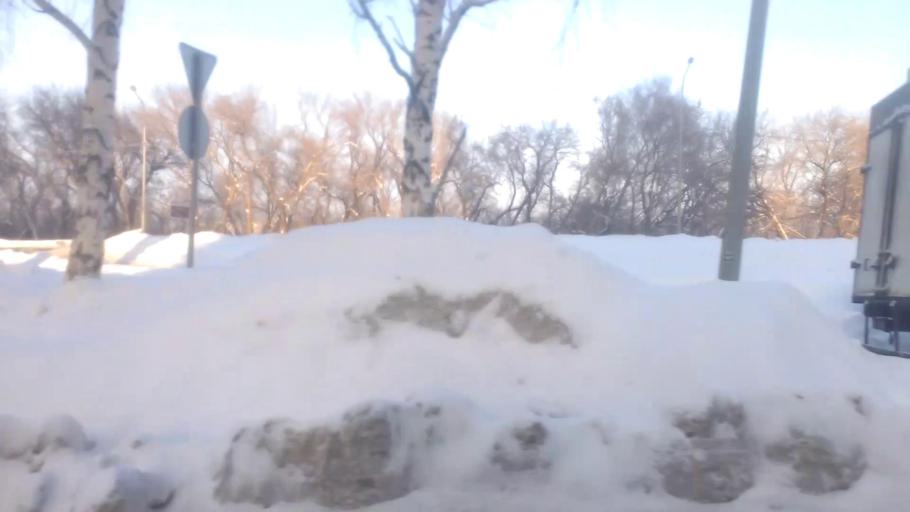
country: RU
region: Altai Krai
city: Novosilikatnyy
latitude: 53.3460
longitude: 83.6518
